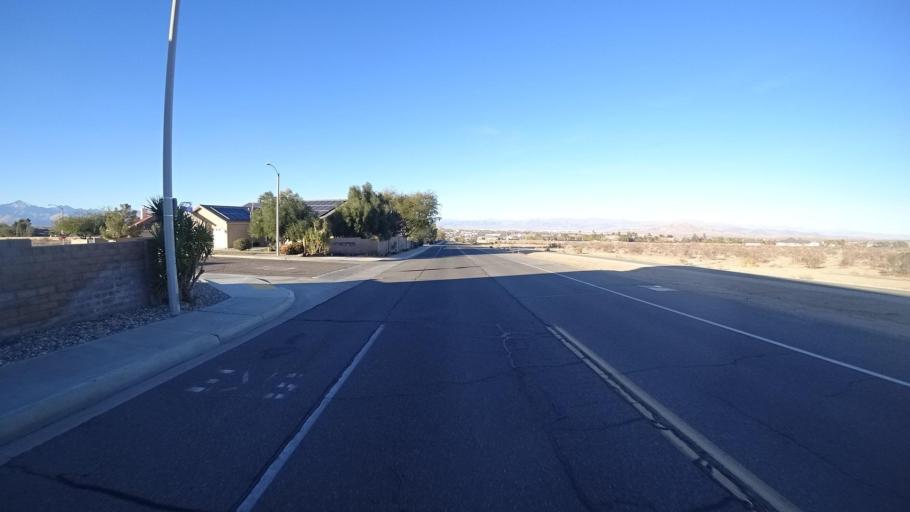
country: US
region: California
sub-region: Kern County
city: Ridgecrest
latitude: 35.5795
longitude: -117.6702
